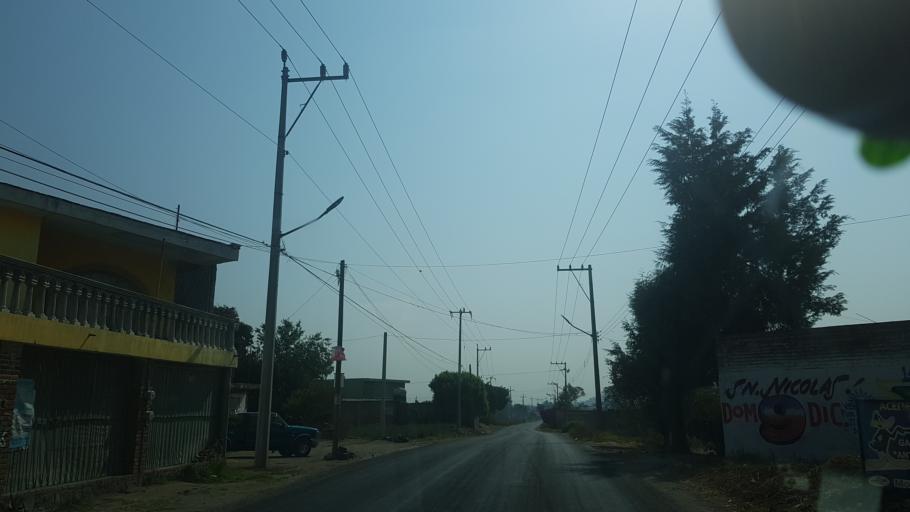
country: MX
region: Puebla
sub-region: San Jeronimo Tecuanipan
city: Los Reyes Tlanechicolpan
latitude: 19.0542
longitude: -98.3367
